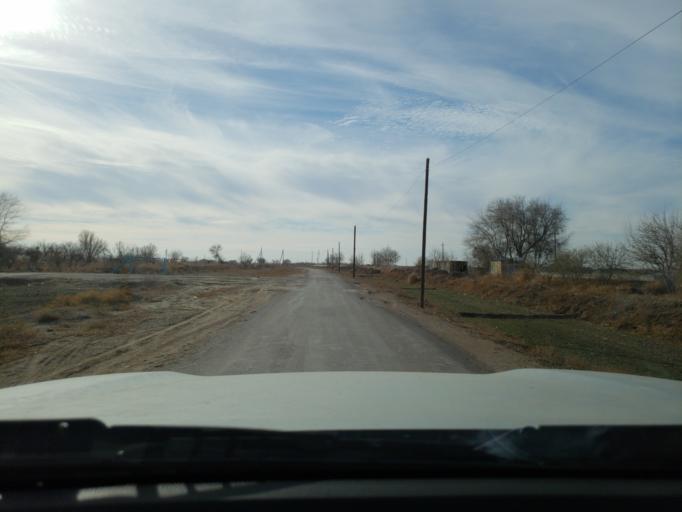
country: TM
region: Dasoguz
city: Dasoguz
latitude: 41.8444
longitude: 59.8739
